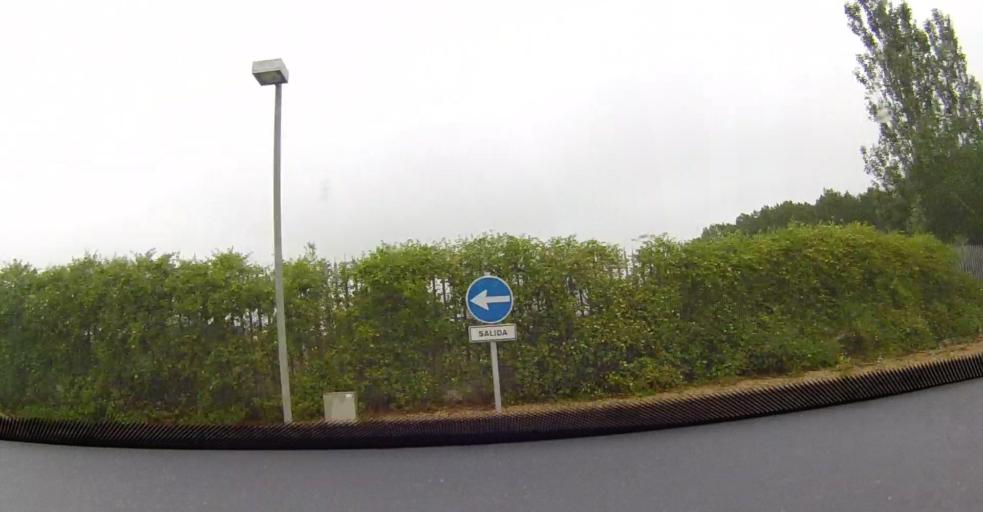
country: ES
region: Castille and Leon
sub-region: Provincia de Palencia
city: Pedrosa de la Vega
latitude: 42.4807
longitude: -4.7366
